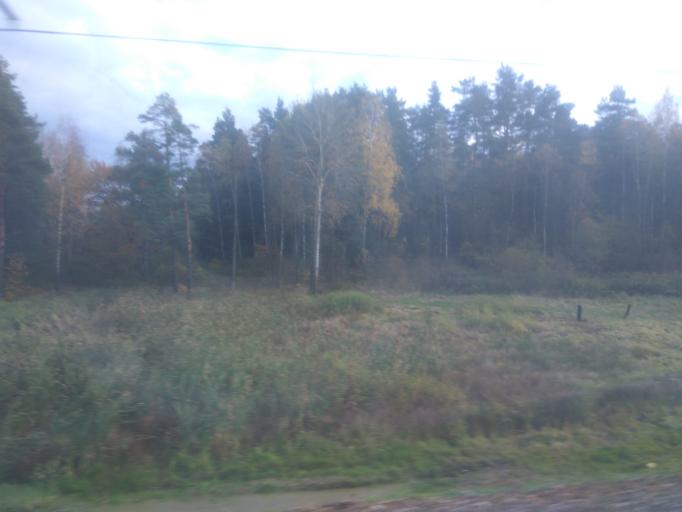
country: RU
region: Moskovskaya
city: Odintsovo
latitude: 55.6470
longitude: 37.2523
